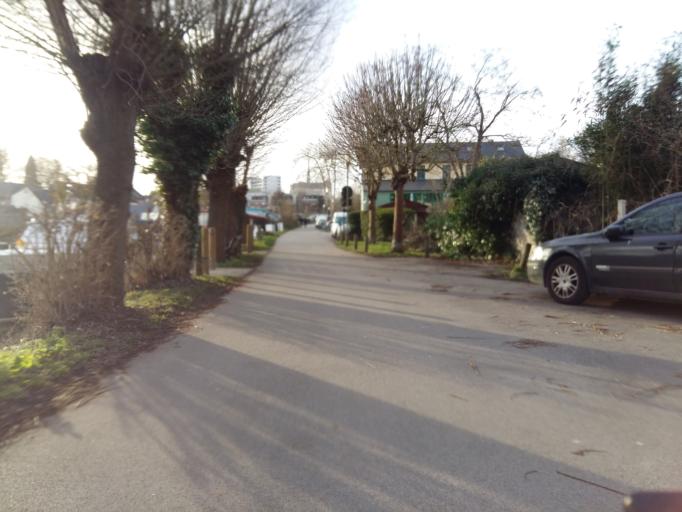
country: FR
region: Picardie
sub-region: Departement de la Somme
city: Rivery
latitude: 49.8944
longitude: 2.3161
